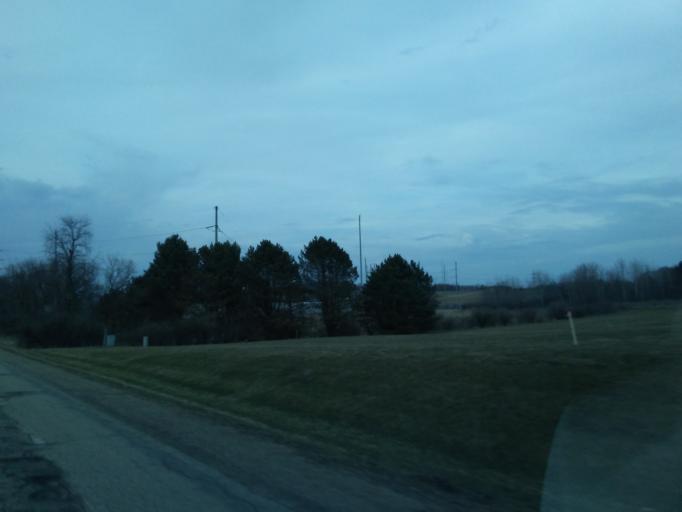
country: US
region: Wisconsin
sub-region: Dane County
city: Verona
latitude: 43.0138
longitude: -89.5336
